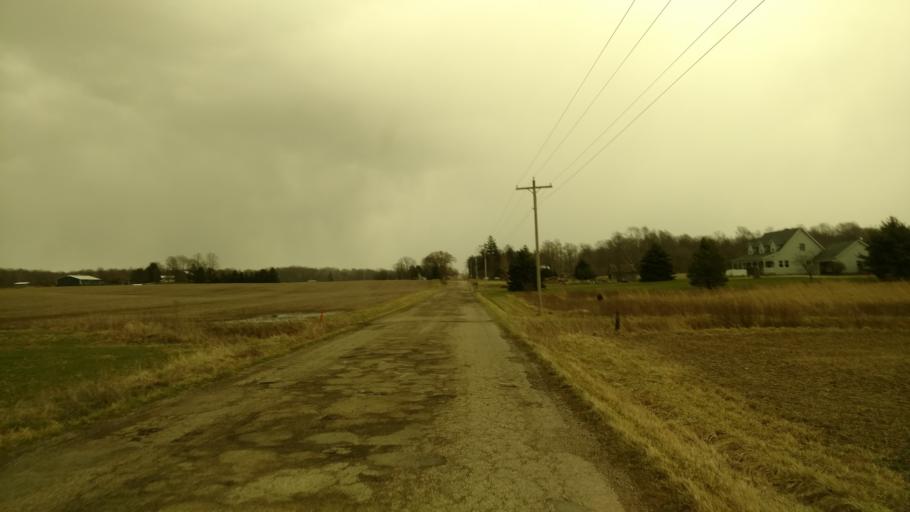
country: US
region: Ohio
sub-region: Morrow County
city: Mount Gilead
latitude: 40.5738
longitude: -82.7868
